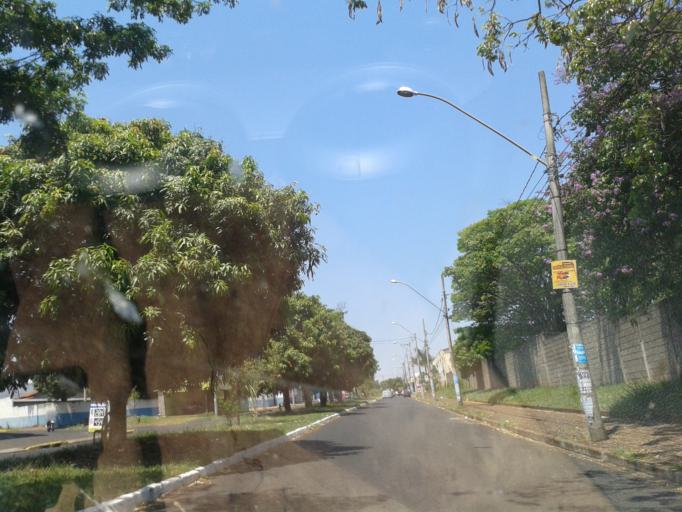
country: BR
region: Minas Gerais
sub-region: Uberlandia
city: Uberlandia
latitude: -18.9358
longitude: -48.3053
